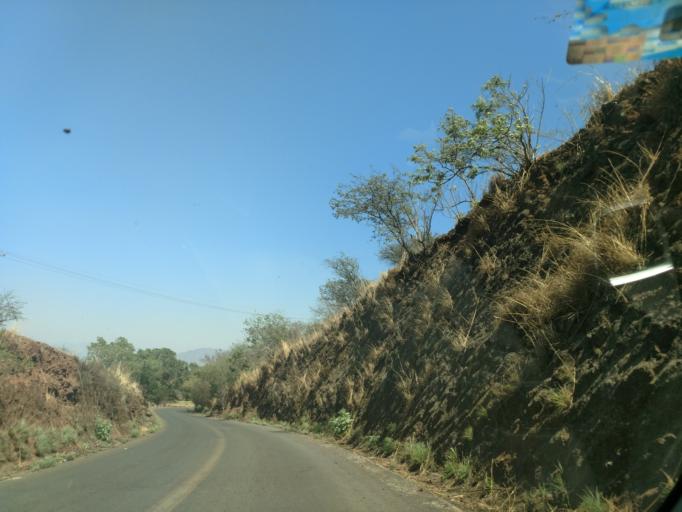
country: MX
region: Nayarit
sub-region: Tepic
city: La Corregidora
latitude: 21.4759
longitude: -104.6724
